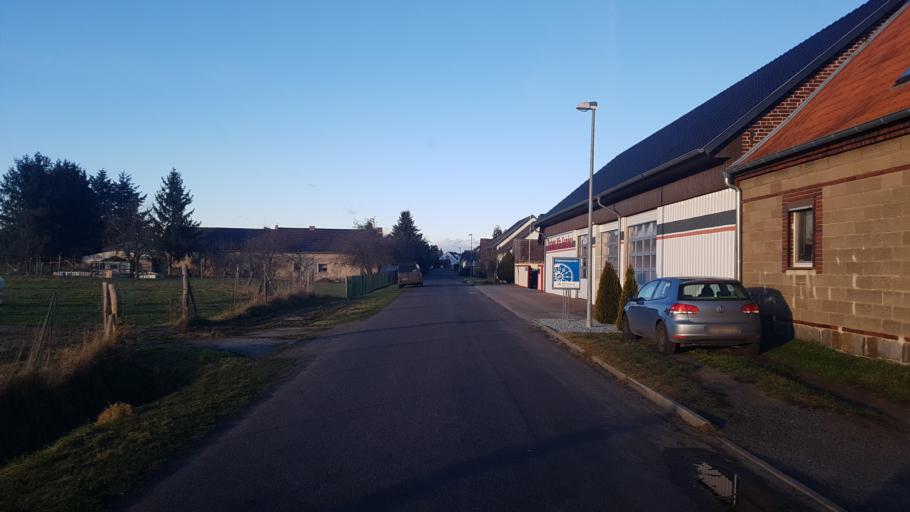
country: DE
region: Brandenburg
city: Drachhausen
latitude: 51.8870
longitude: 14.3195
